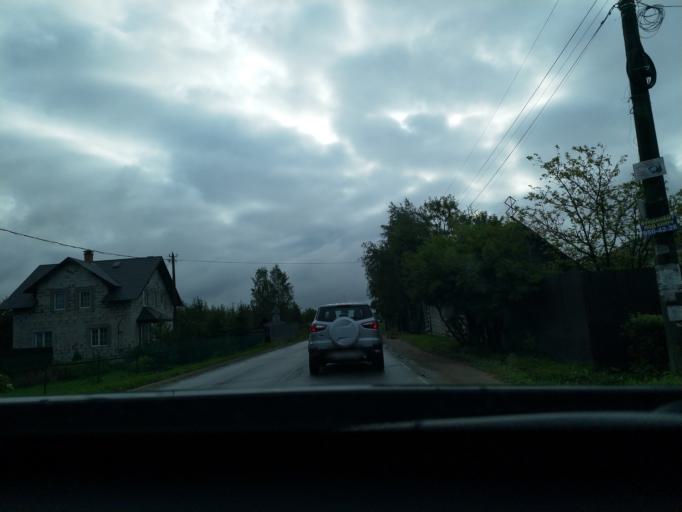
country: RU
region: Leningrad
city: Nikol'skoye
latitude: 59.6919
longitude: 30.7864
